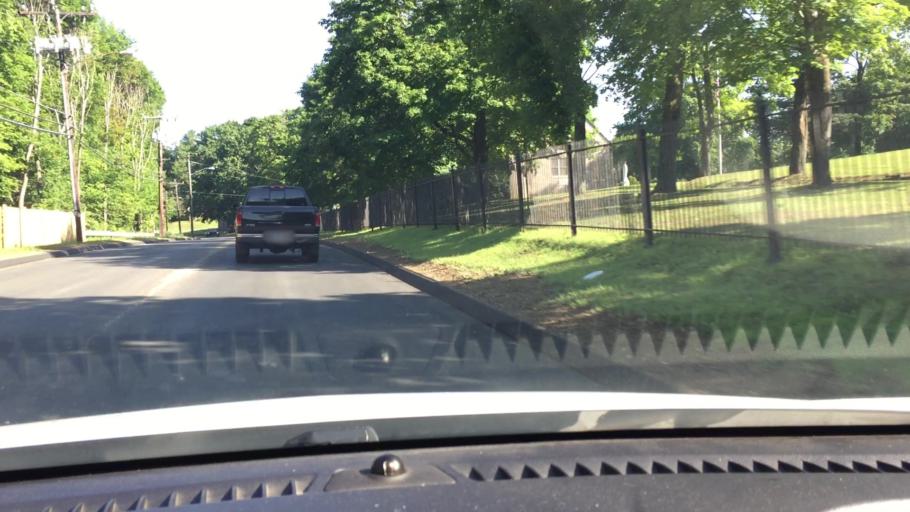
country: US
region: Massachusetts
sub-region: Berkshire County
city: Pittsfield
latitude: 42.4718
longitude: -73.2589
